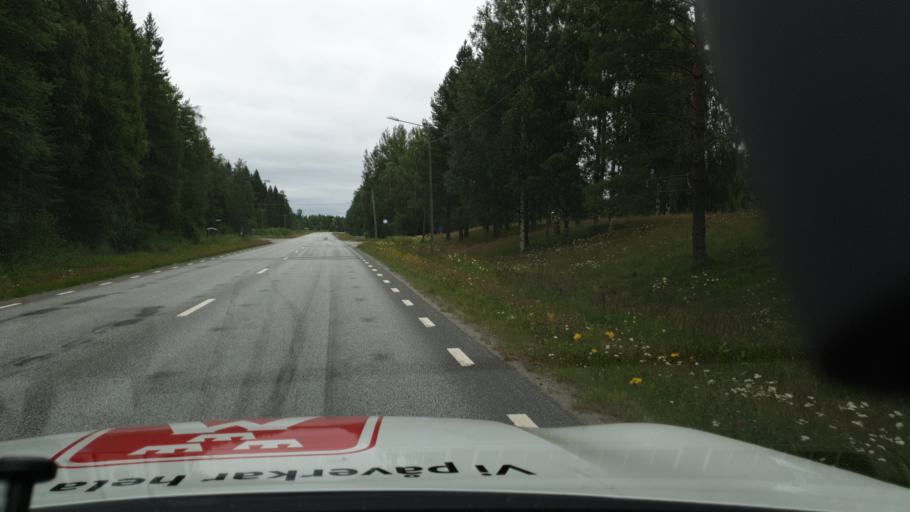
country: SE
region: Vaesterbotten
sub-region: Umea Kommun
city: Ersmark
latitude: 63.8795
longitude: 20.3069
